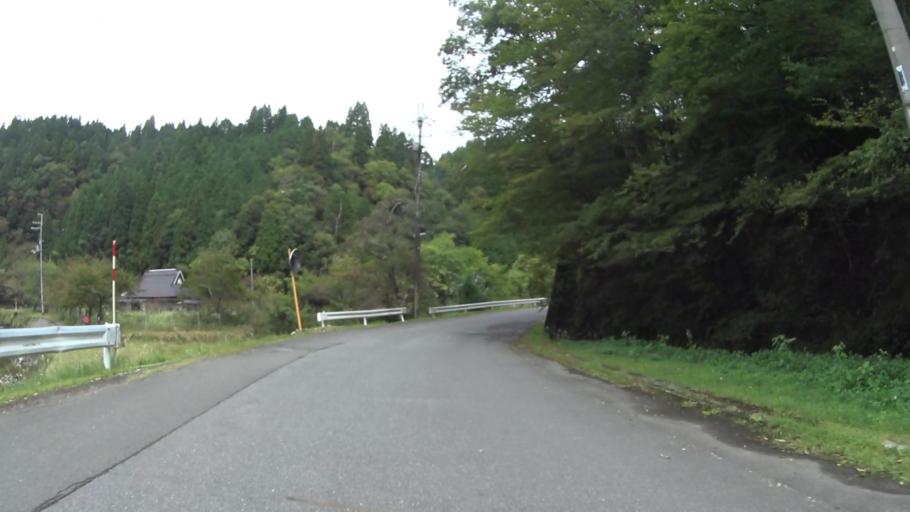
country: JP
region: Shiga Prefecture
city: Kitahama
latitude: 35.2591
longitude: 135.7522
